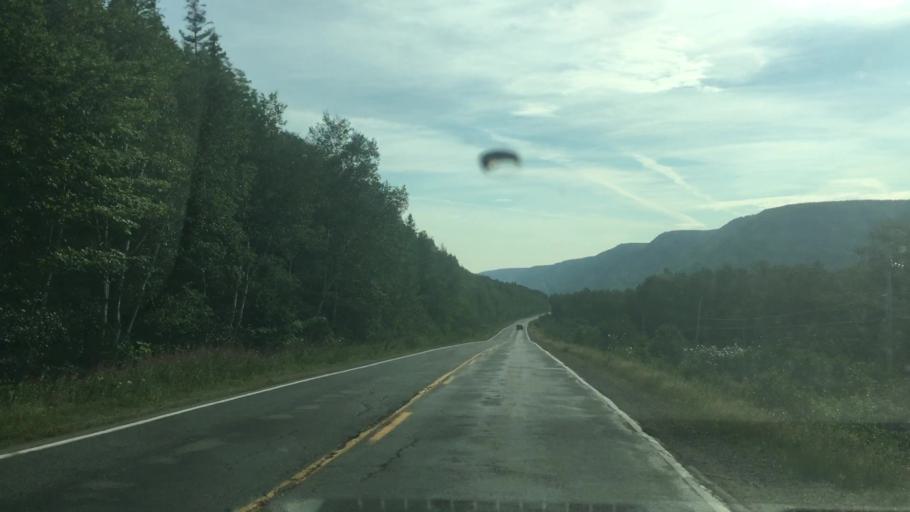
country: CA
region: Nova Scotia
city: Sydney Mines
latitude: 46.8645
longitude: -60.5620
